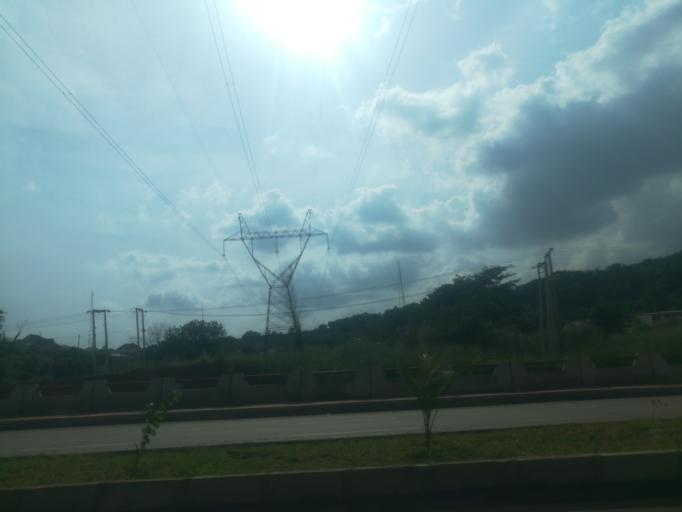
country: NG
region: Ogun
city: Abeokuta
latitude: 7.1275
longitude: 3.3562
